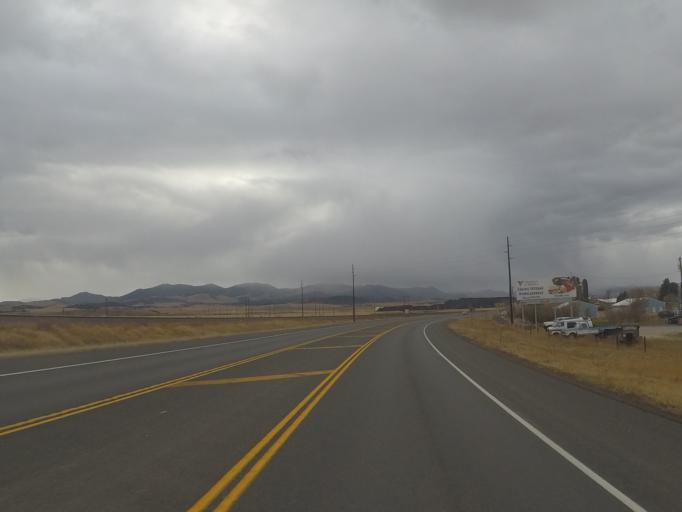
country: US
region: Montana
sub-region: Lewis and Clark County
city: East Helena
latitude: 46.5860
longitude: -111.8977
